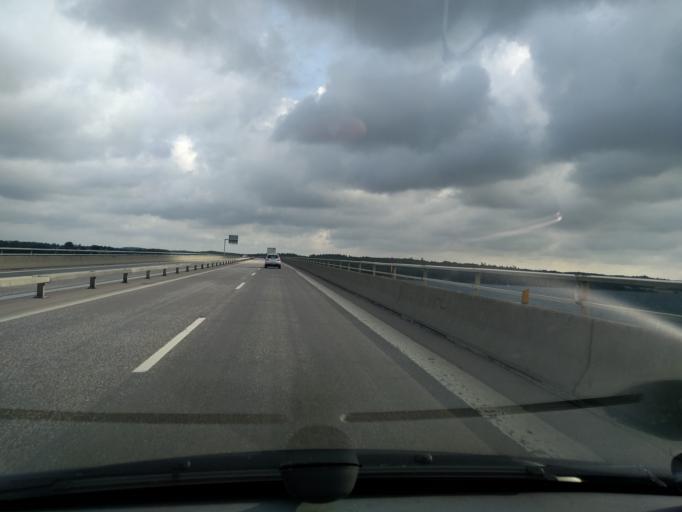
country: DK
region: Zealand
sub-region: Vordingborg Kommune
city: Nyrad
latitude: 54.9593
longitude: 11.9952
